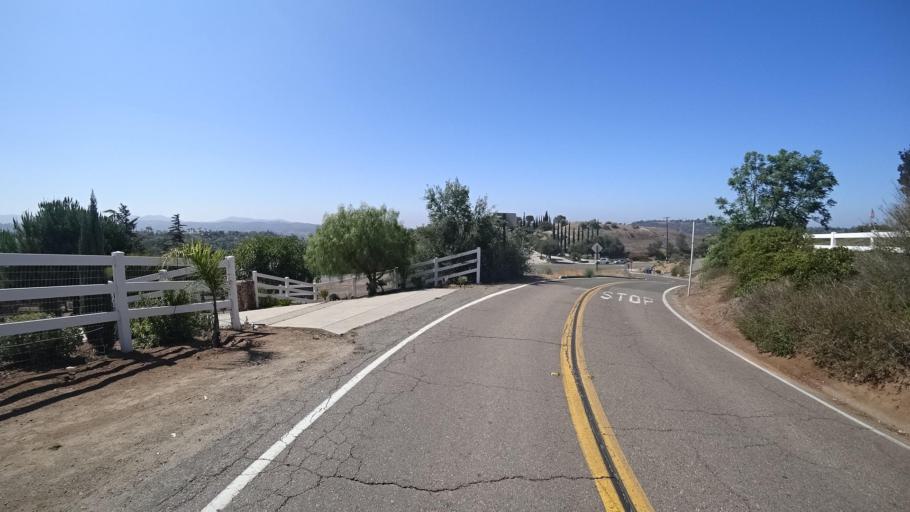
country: US
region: California
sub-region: San Diego County
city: Bonsall
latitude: 33.3187
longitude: -117.2201
